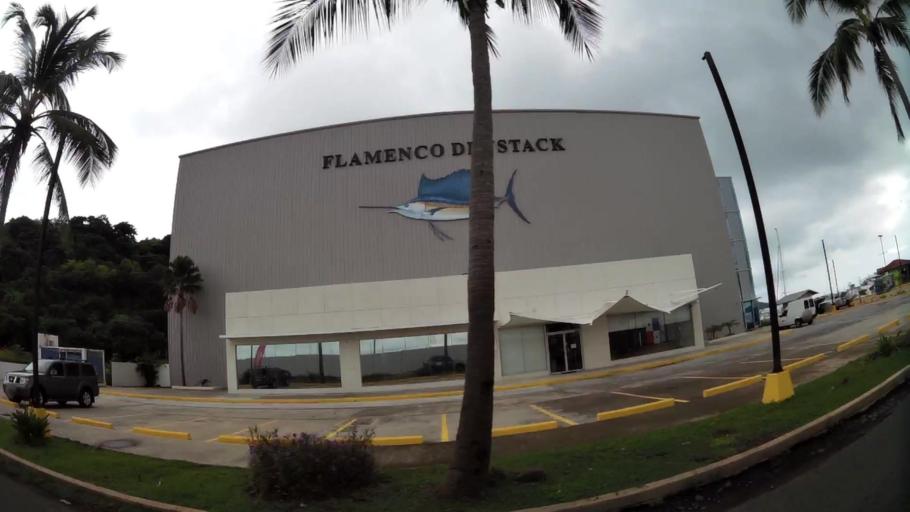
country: PA
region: Panama
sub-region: Distrito de Panama
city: Ancon
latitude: 8.9118
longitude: -79.5238
